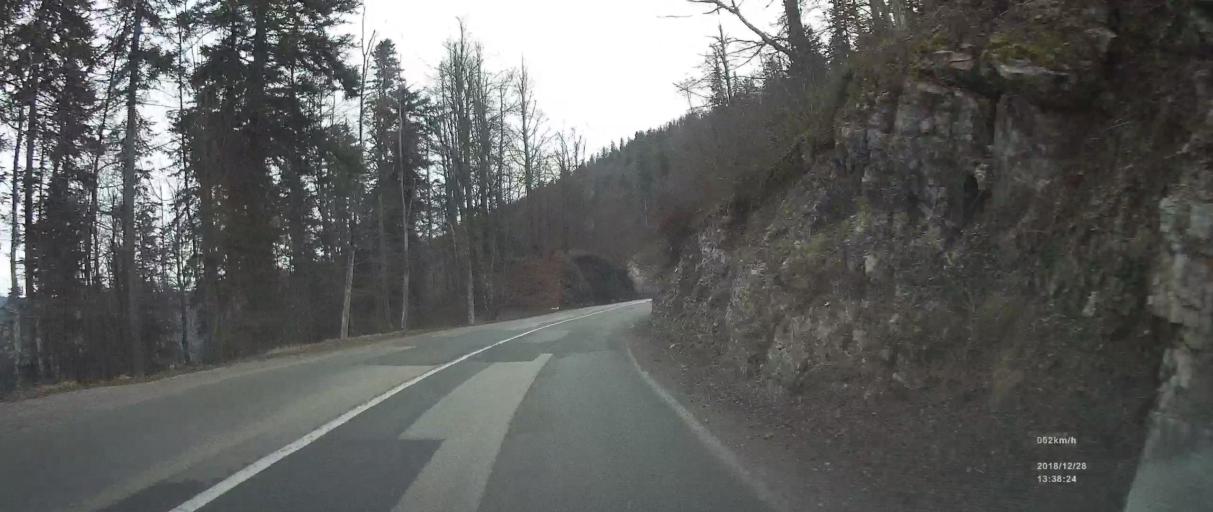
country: HR
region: Primorsko-Goranska
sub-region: Grad Delnice
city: Delnice
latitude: 45.3560
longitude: 14.7246
